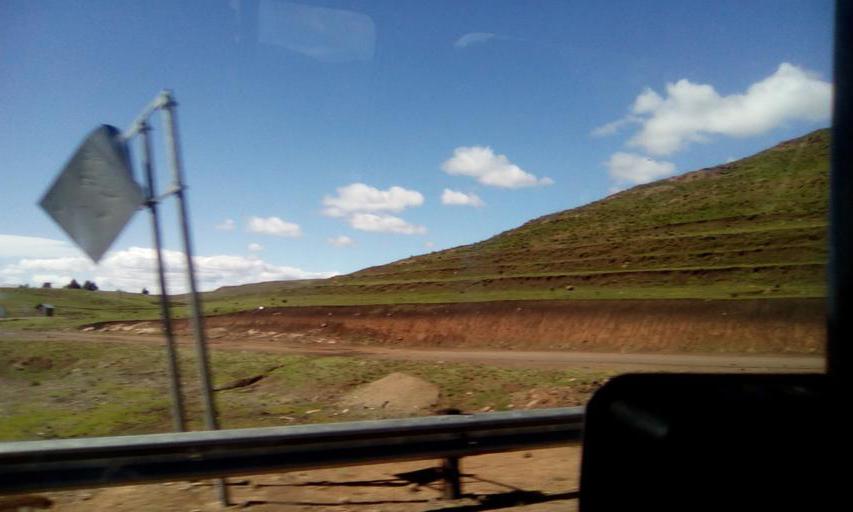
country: LS
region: Maseru
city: Nako
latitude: -29.8260
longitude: 28.0360
